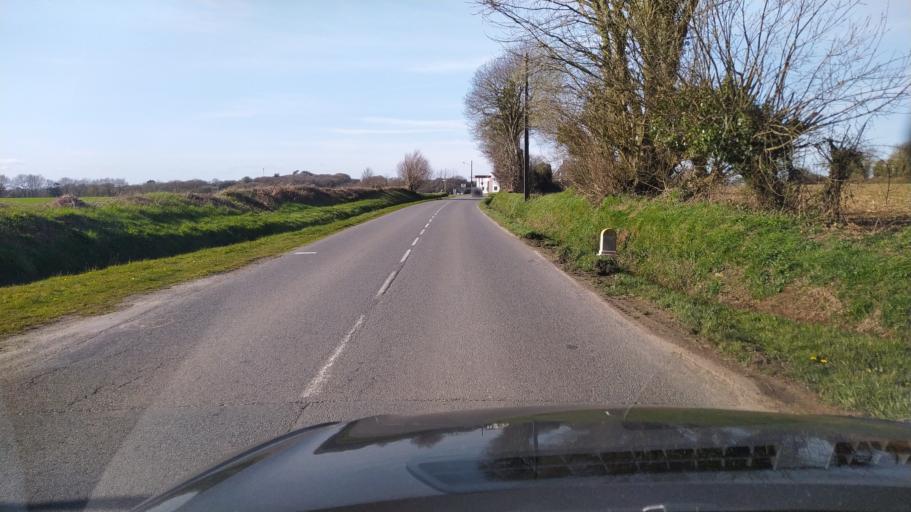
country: FR
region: Brittany
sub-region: Departement du Finistere
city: Lampaul-Guimiliau
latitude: 48.4512
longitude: -4.0096
